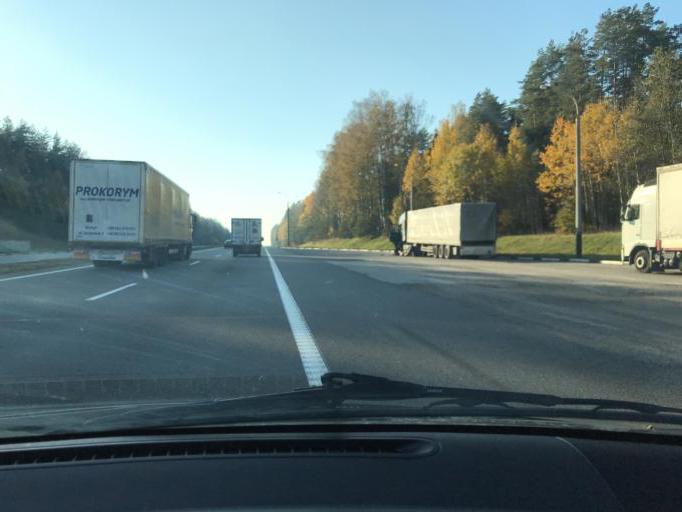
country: BY
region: Minsk
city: Loshnitsa
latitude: 54.3006
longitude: 28.9493
